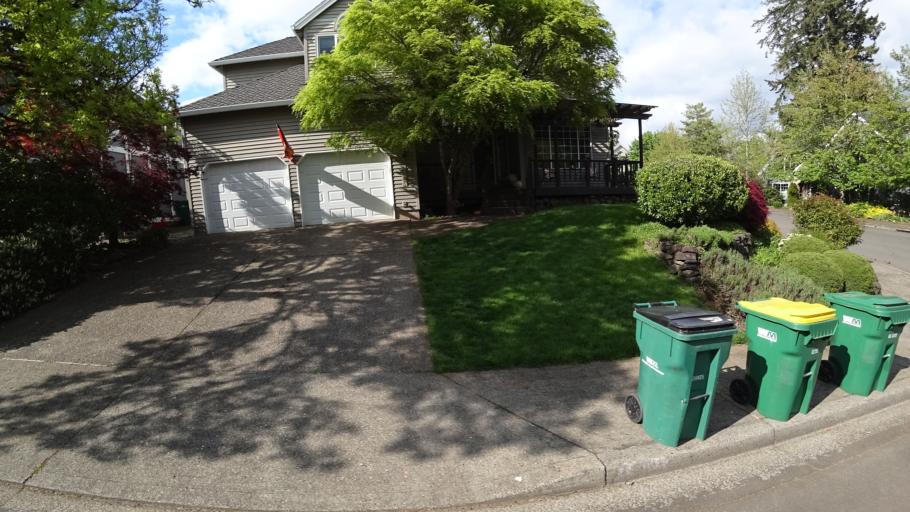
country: US
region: Oregon
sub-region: Washington County
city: Beaverton
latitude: 45.4472
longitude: -122.8339
